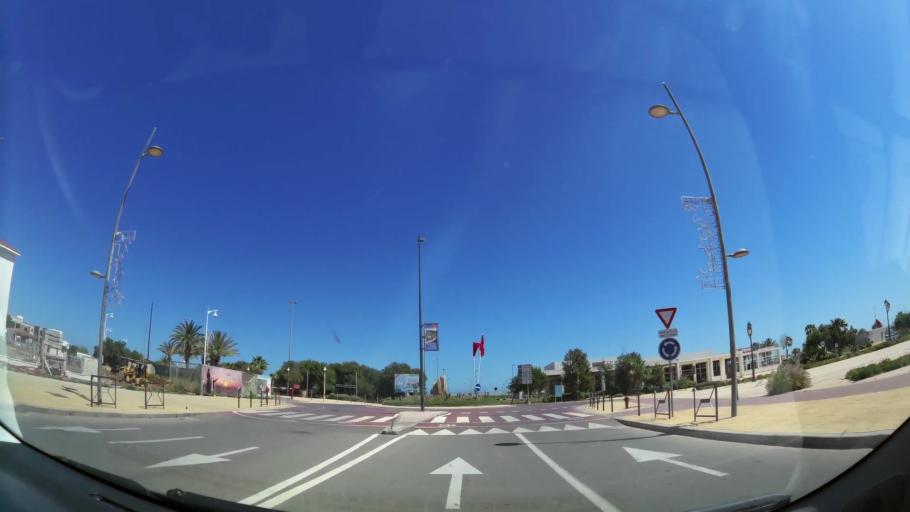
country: MA
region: Oriental
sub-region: Berkane-Taourirt
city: Madagh
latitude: 35.1089
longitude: -2.2996
